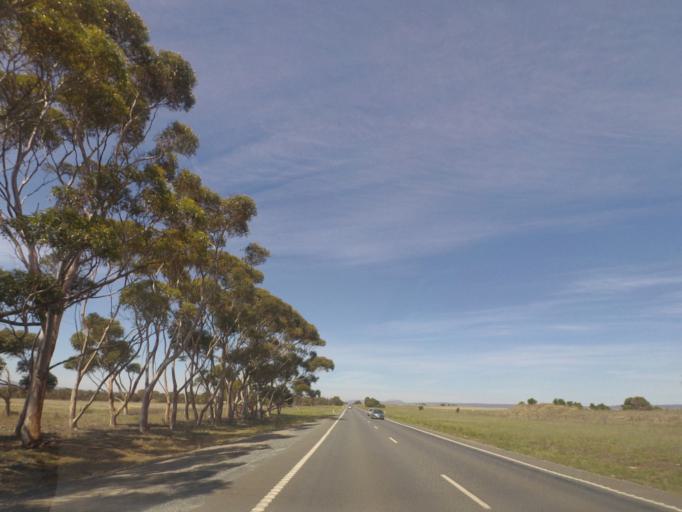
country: AU
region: Victoria
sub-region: Moorabool
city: Bacchus Marsh
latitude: -37.7838
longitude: 144.4276
